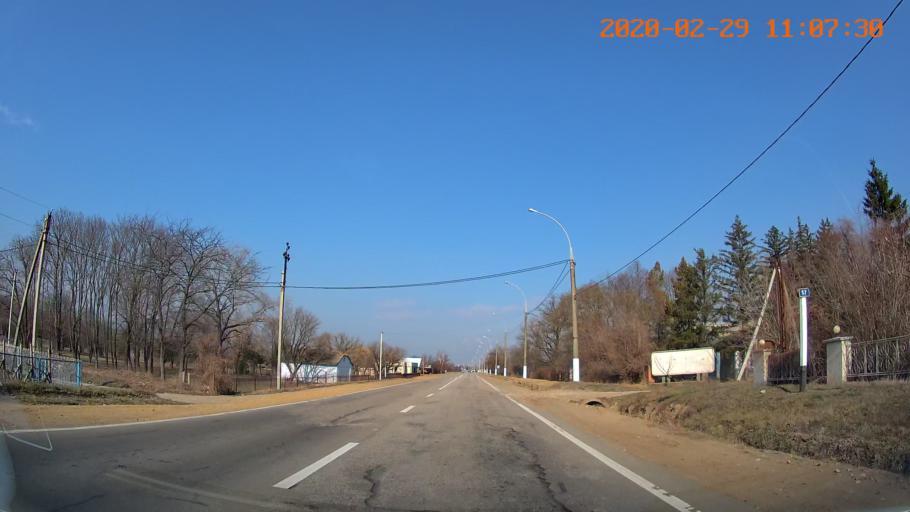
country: MD
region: Criuleni
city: Criuleni
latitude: 47.2258
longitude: 29.1817
